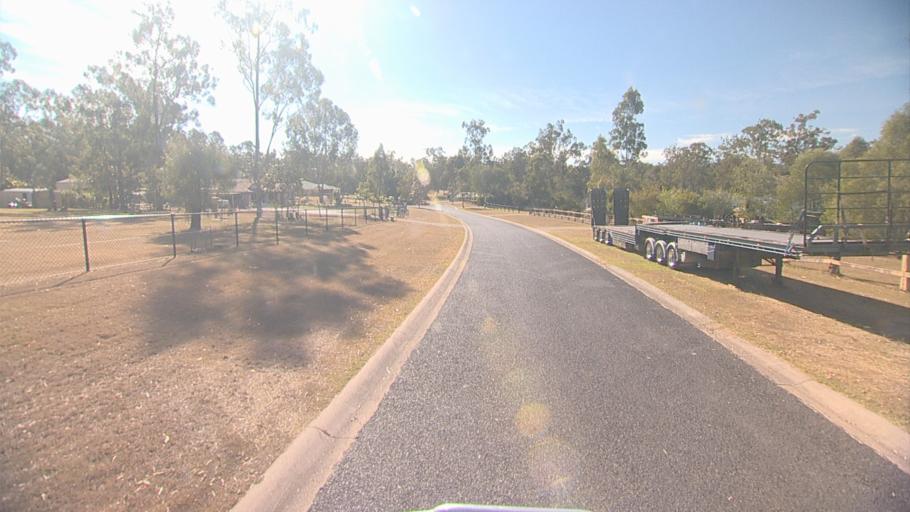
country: AU
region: Queensland
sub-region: Logan
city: North Maclean
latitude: -27.7989
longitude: 152.9744
